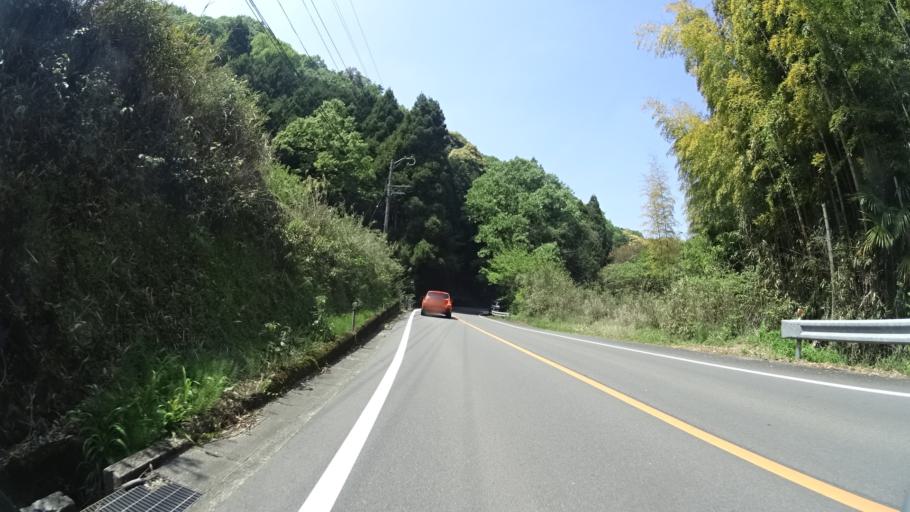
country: JP
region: Ehime
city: Hojo
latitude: 33.9699
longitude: 132.9028
